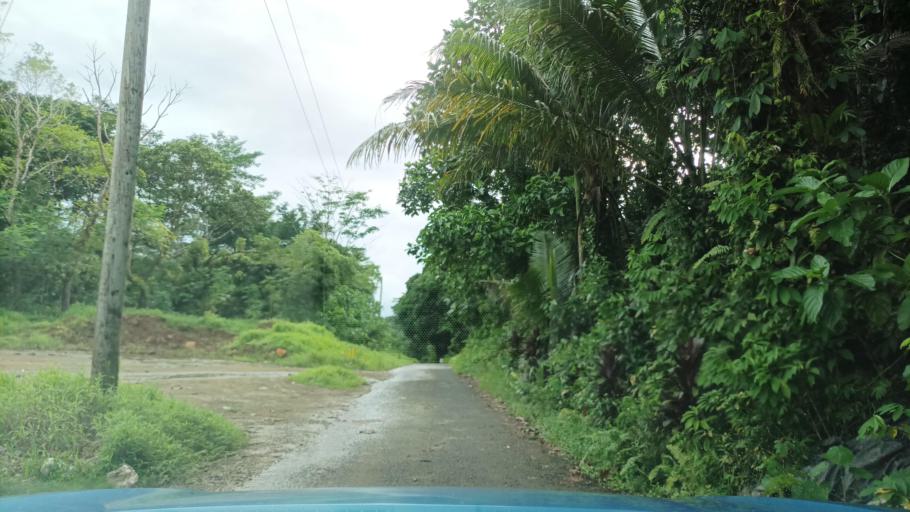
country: FM
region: Pohnpei
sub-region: Sokehs Municipality
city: Palikir - National Government Center
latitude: 6.8805
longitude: 158.1675
